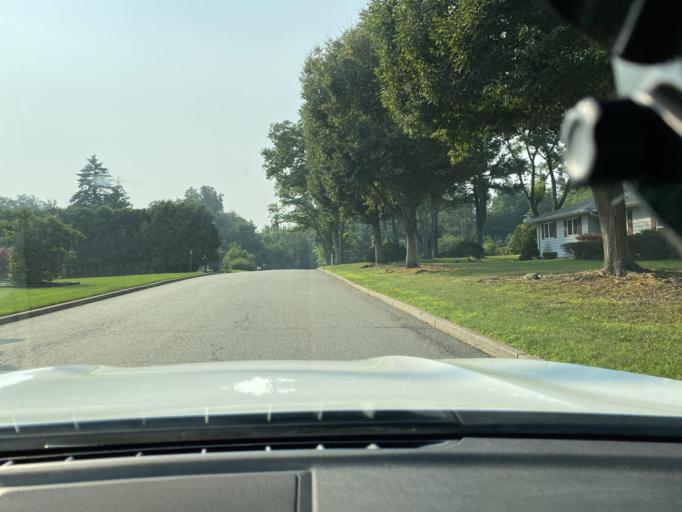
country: US
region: New York
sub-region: Rockland County
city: Airmont
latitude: 41.0933
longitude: -74.1198
